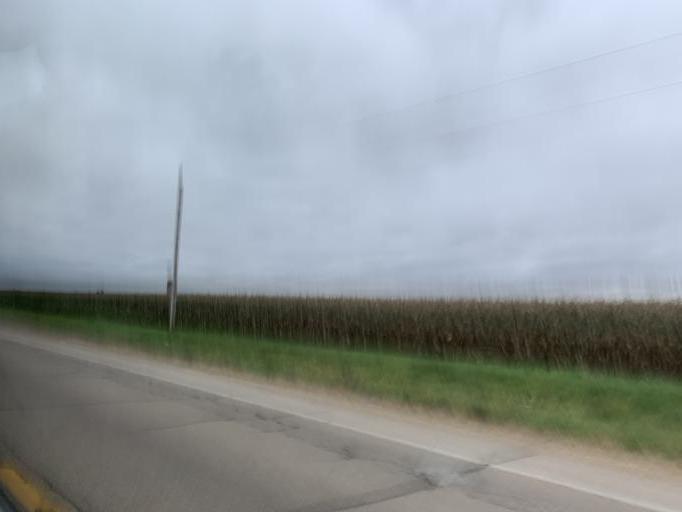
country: US
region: Wisconsin
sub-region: Grant County
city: Muscoda
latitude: 43.2197
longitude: -90.4785
